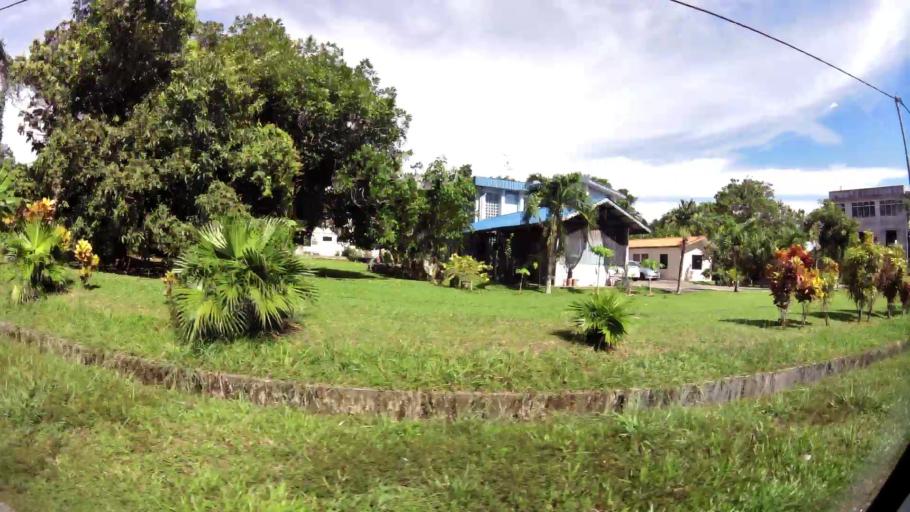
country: BN
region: Brunei and Muara
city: Bandar Seri Begawan
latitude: 5.0291
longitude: 115.0505
